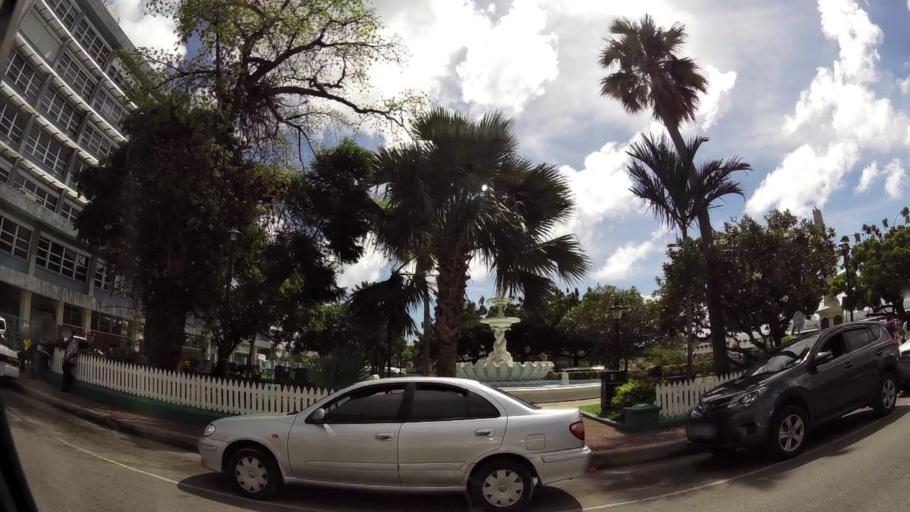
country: BB
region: Saint Michael
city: Bridgetown
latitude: 13.0969
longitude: -59.6138
